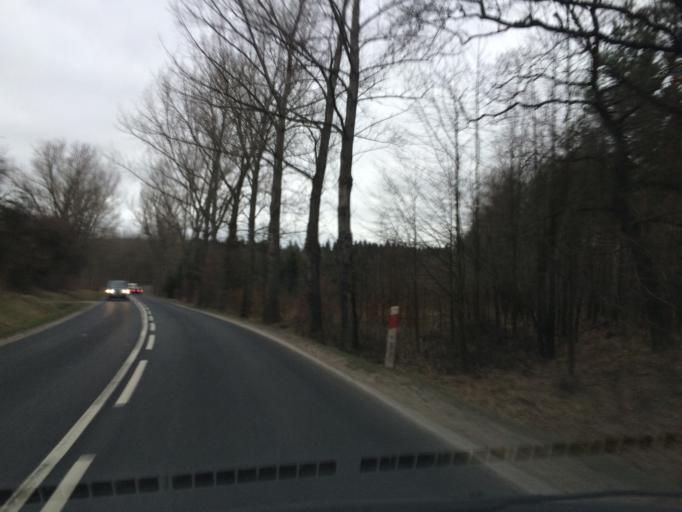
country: PL
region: Lower Silesian Voivodeship
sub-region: Powiat lubanski
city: Luban
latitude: 51.1428
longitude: 15.2740
